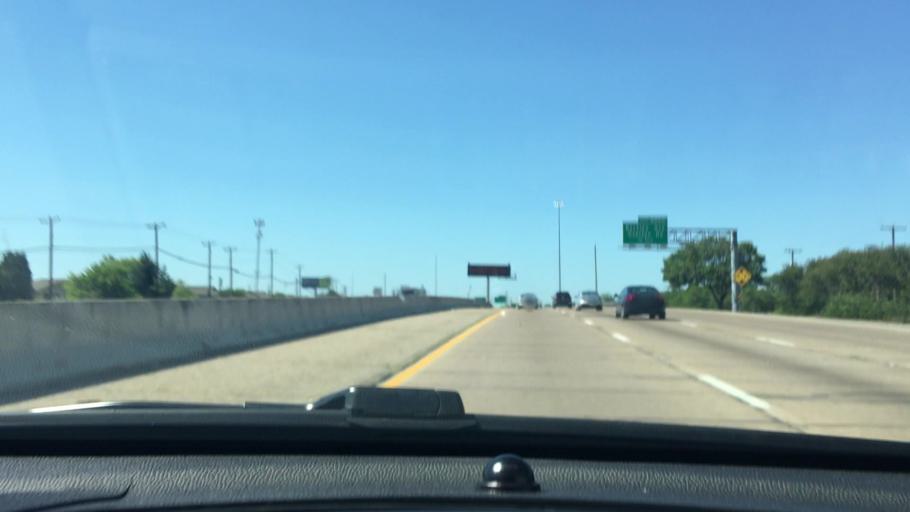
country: US
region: Texas
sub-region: Dallas County
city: Cockrell Hill
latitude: 32.6949
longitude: -96.8232
